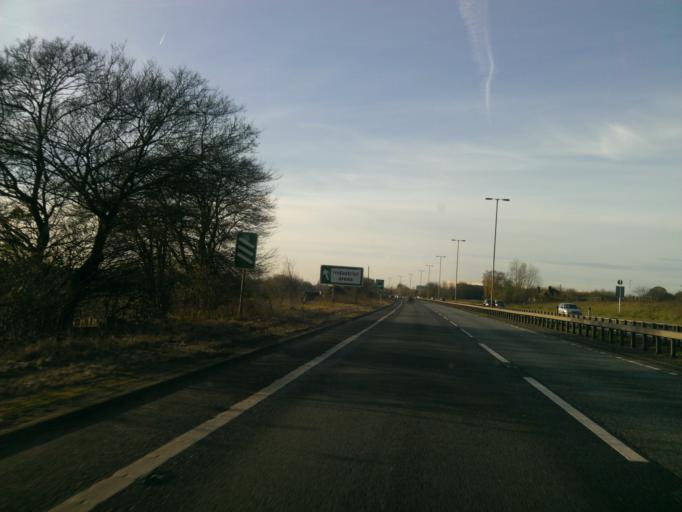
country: GB
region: England
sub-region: Essex
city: Witham
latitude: 51.8142
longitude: 0.6607
